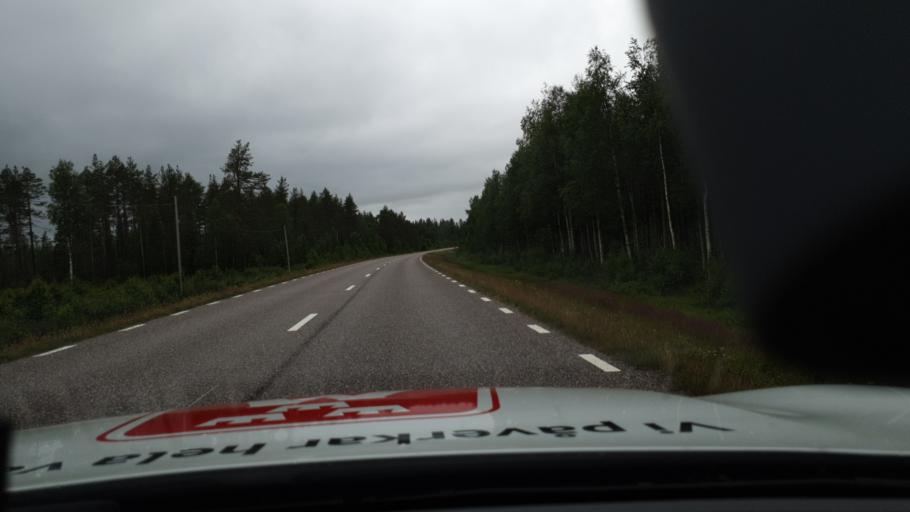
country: FI
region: Lapland
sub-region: Tunturi-Lappi
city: Kolari
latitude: 67.0128
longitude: 23.7379
